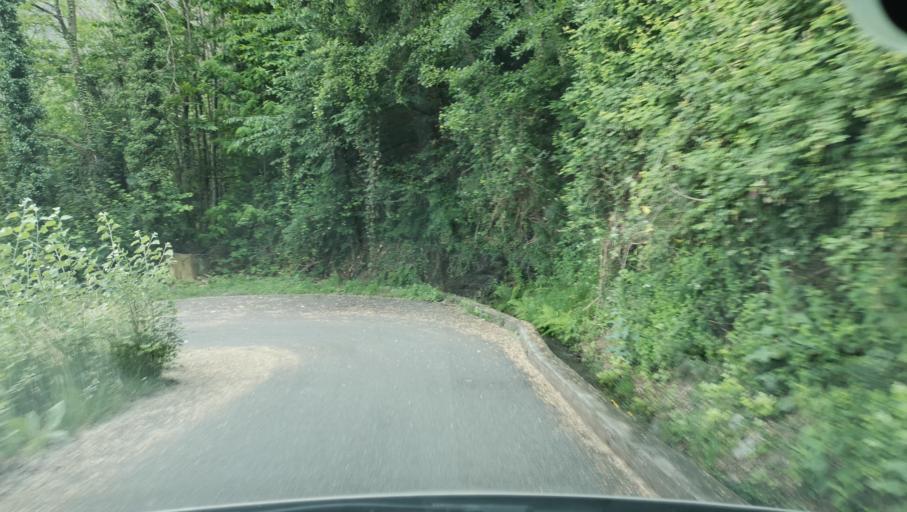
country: IT
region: Piedmont
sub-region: Provincia di Torino
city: Quassolo
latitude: 45.5272
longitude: 7.8258
